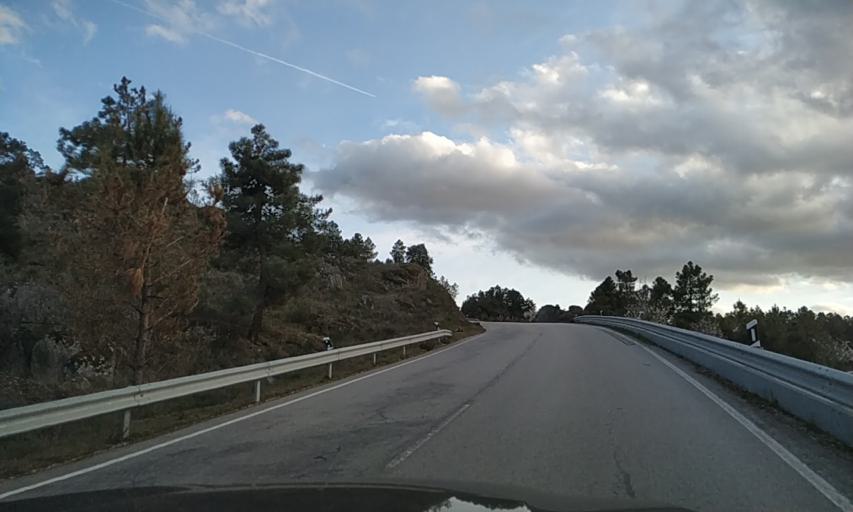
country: PT
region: Braganca
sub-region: Carrazeda de Ansiaes
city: Carrazeda de Anciaes
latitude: 41.2851
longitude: -7.3374
